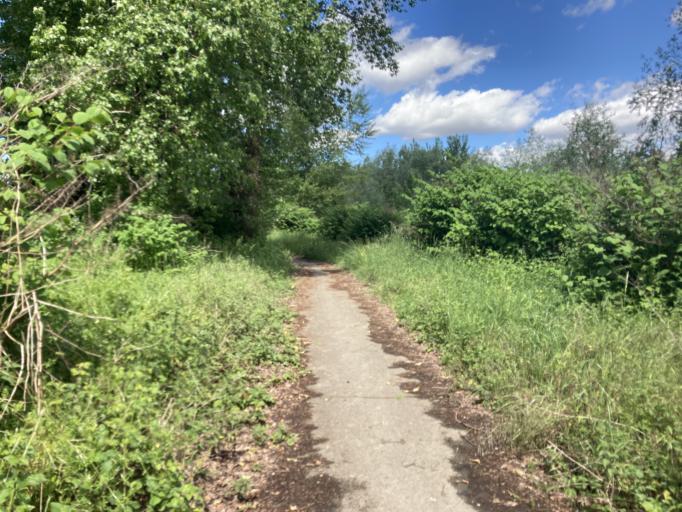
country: FR
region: Aquitaine
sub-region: Departement des Pyrenees-Atlantiques
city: Arbus
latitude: 43.3395
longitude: -0.4994
